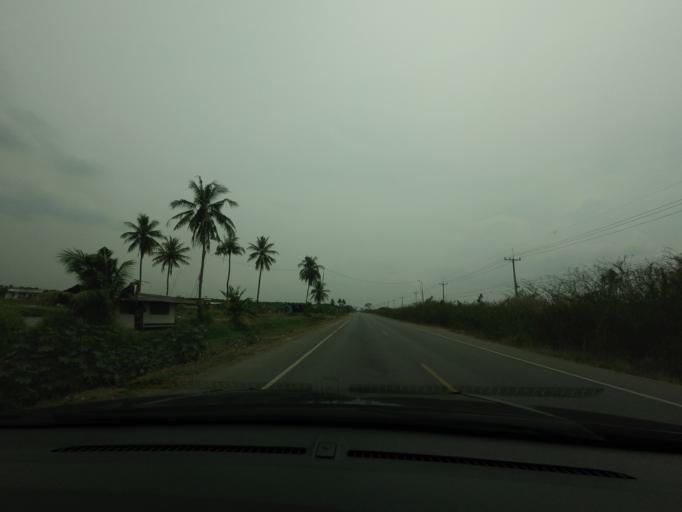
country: TH
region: Phetchaburi
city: Ban Laem
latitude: 13.1780
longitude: 99.9372
